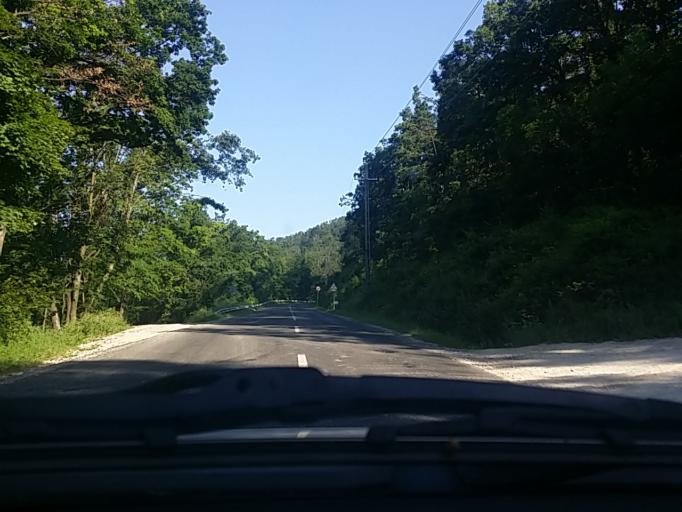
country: HU
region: Pest
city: Pilisszentkereszt
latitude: 47.7102
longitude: 18.8804
